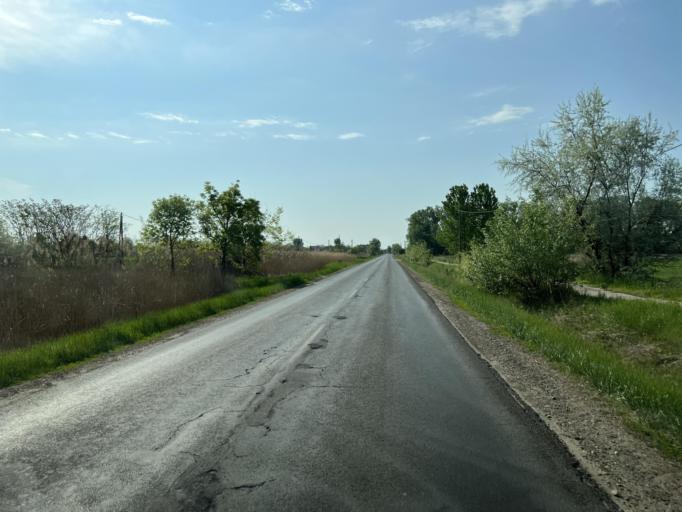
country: HU
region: Pest
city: Jaszkarajeno
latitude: 47.0639
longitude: 20.0554
